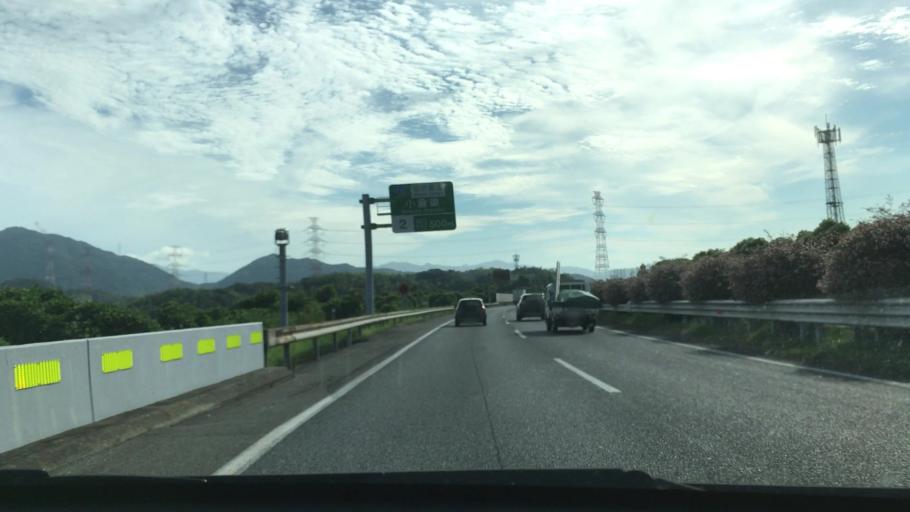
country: JP
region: Fukuoka
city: Kanda
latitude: 33.8346
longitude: 130.9194
